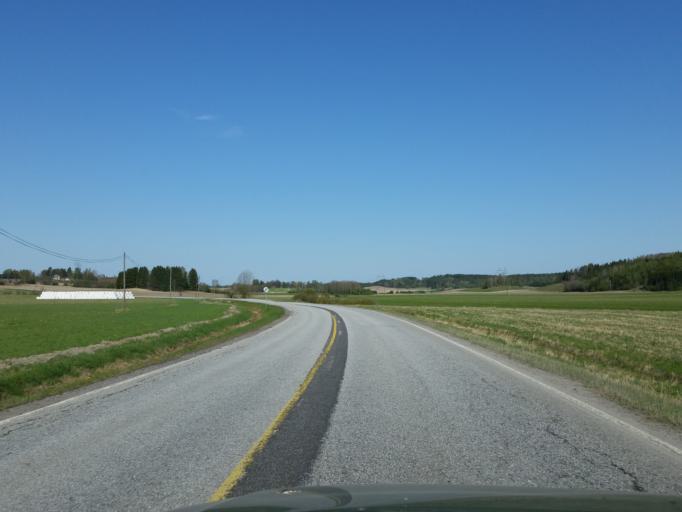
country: FI
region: Uusimaa
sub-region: Helsinki
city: Siuntio
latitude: 60.1737
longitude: 24.1609
